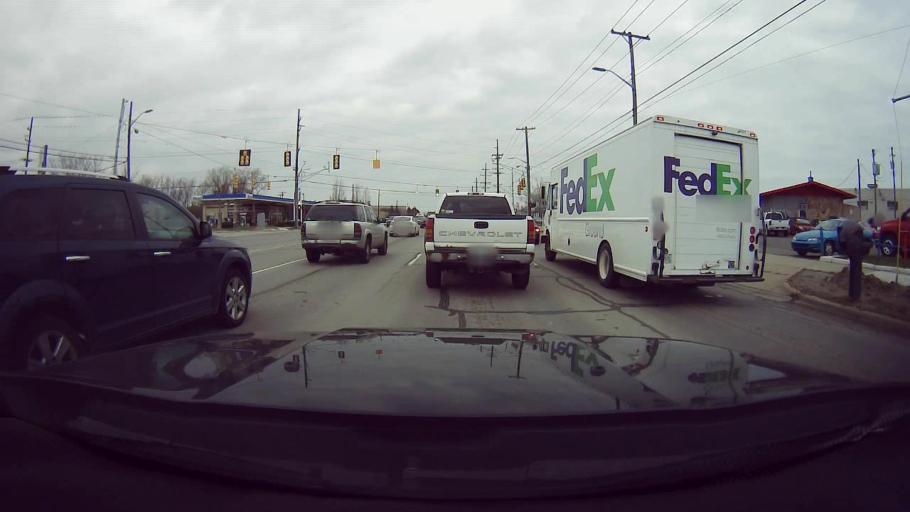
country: US
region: Michigan
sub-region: Macomb County
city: Eastpointe
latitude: 42.4782
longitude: -82.9808
